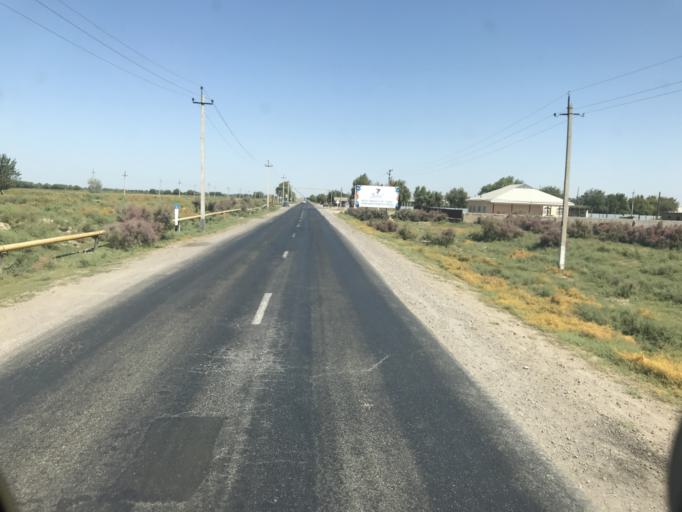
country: KZ
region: Ongtustik Qazaqstan
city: Ilyich
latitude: 40.8951
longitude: 68.4882
